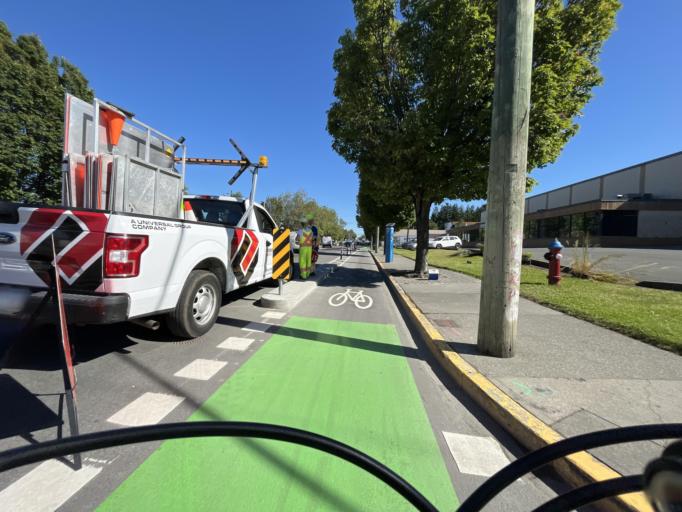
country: CA
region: British Columbia
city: Victoria
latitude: 48.4336
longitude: -123.3671
